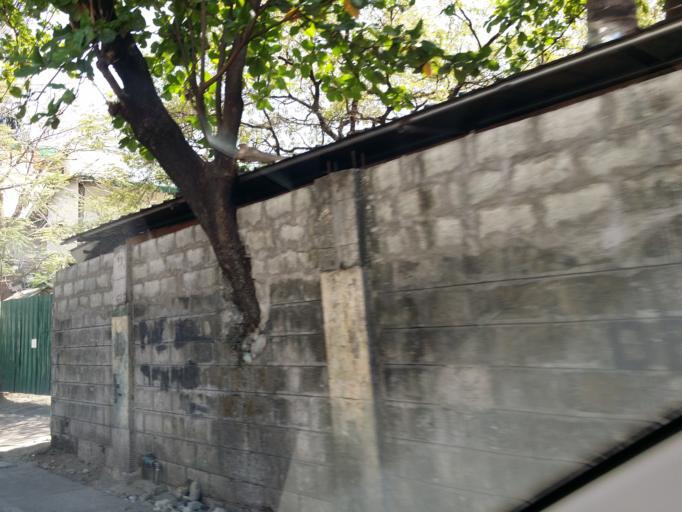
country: PH
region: Metro Manila
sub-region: Mandaluyong
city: Mandaluyong City
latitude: 14.5821
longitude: 121.0250
